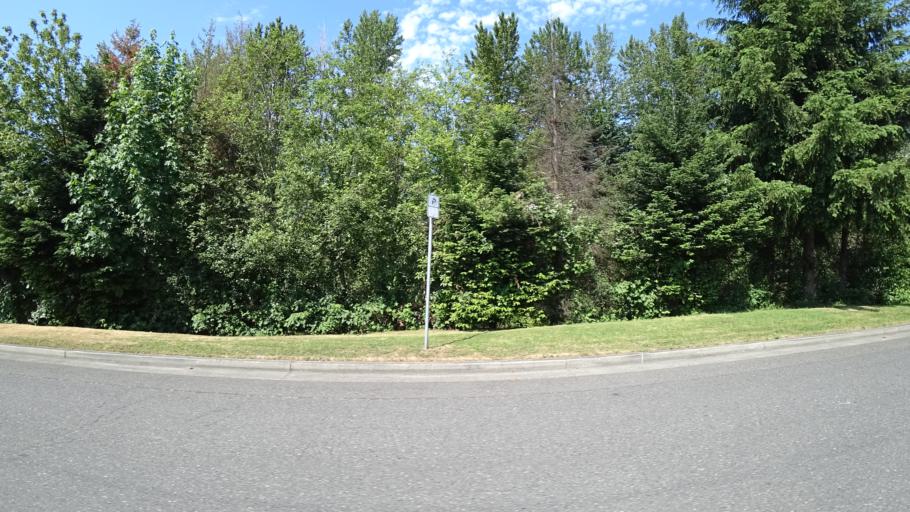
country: US
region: Oregon
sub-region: Multnomah County
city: Lents
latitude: 45.5631
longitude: -122.5370
